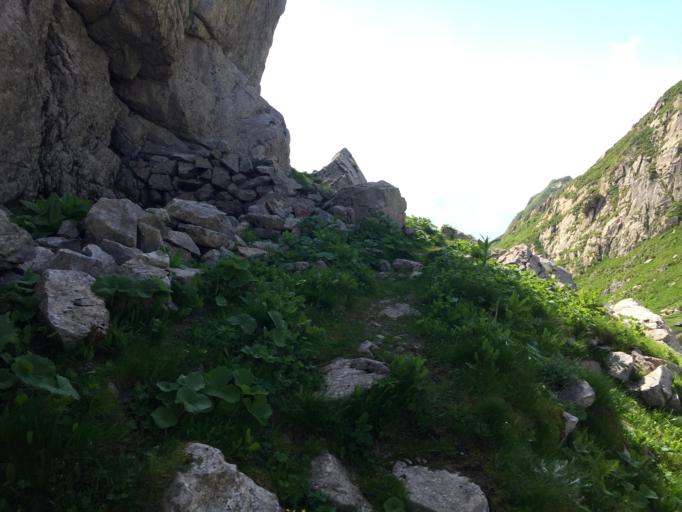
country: IT
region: Friuli Venezia Giulia
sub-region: Provincia di Udine
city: Rigolato
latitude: 46.6138
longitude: 12.8813
